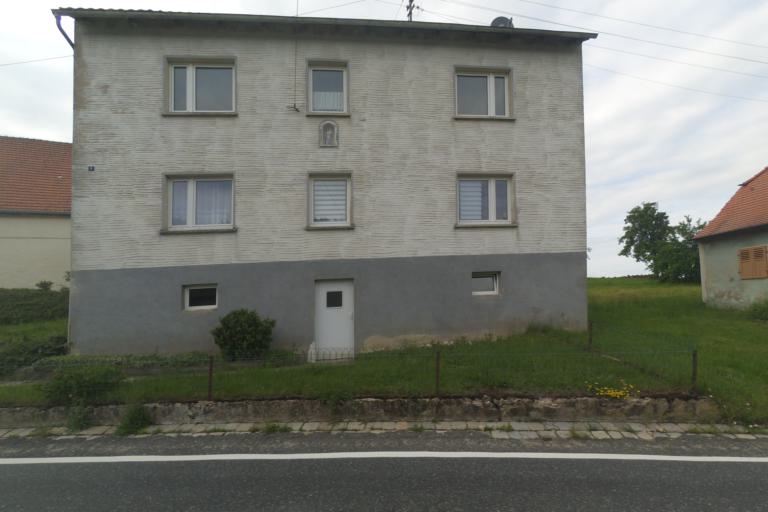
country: DE
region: Bavaria
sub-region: Upper Franconia
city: Schlusselfeld
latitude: 49.7830
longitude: 10.6549
